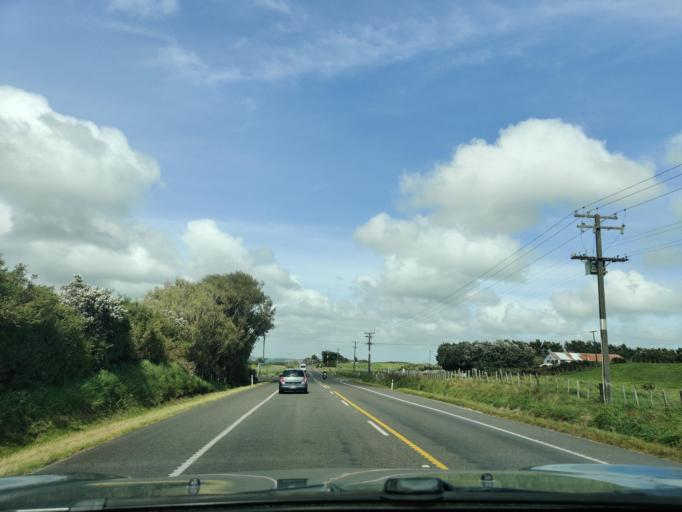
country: NZ
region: Taranaki
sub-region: South Taranaki District
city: Patea
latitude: -39.7731
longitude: 174.6746
